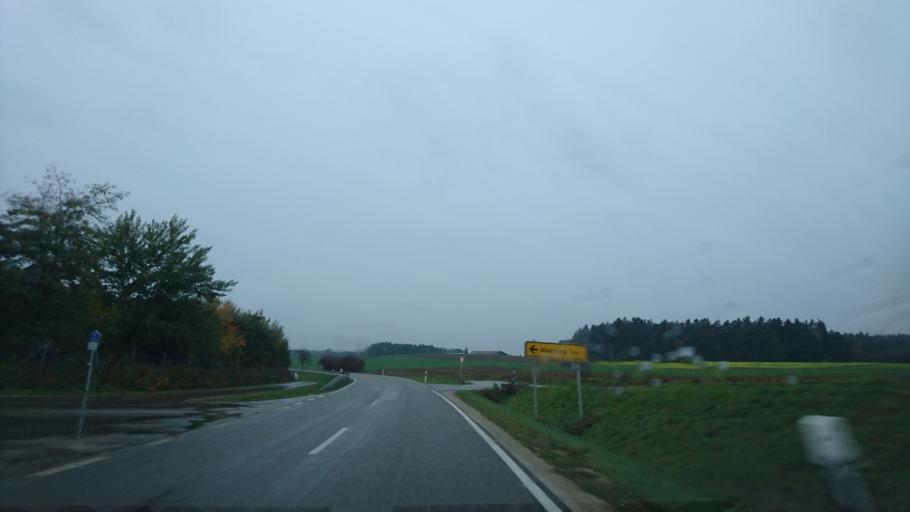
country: DE
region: Bavaria
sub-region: Swabia
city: Kuhbach
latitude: 48.4576
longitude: 11.2018
